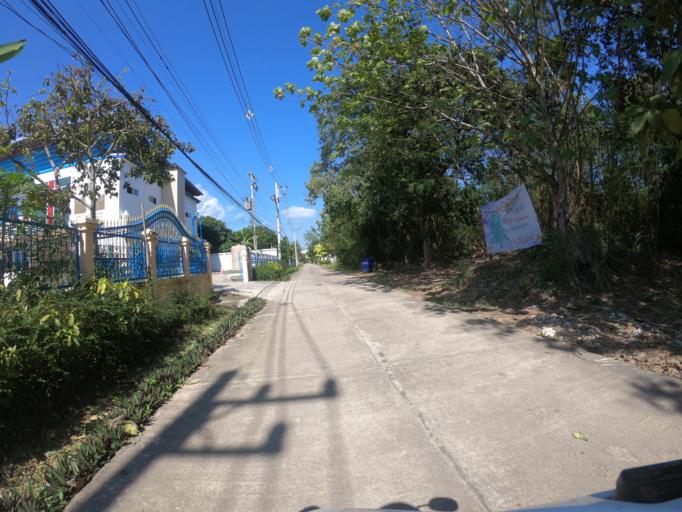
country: TH
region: Chiang Mai
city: Chiang Mai
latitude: 18.7490
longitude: 98.9683
